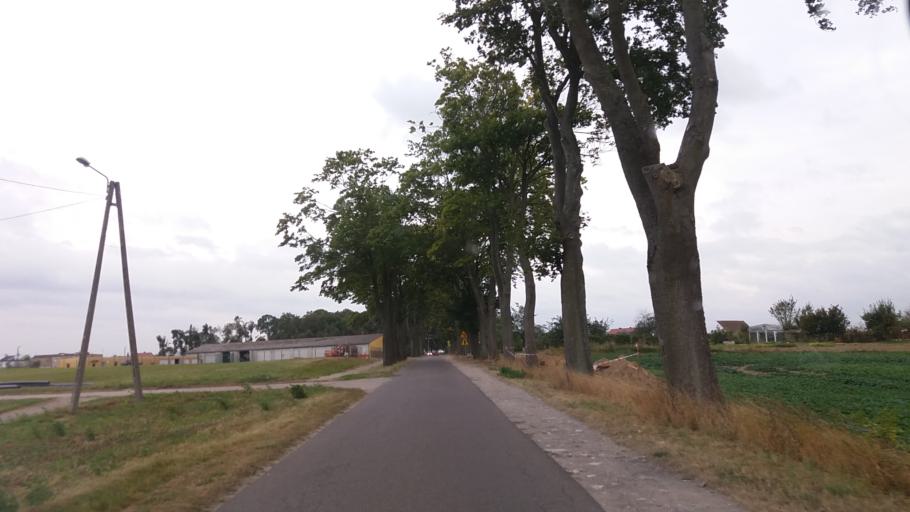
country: PL
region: West Pomeranian Voivodeship
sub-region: Powiat choszczenski
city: Bierzwnik
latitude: 52.9736
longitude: 15.5789
